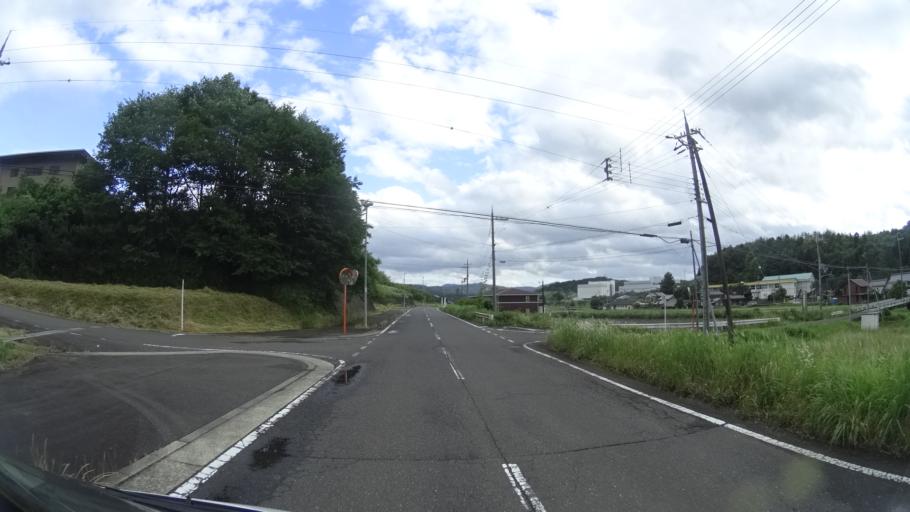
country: JP
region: Kyoto
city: Ayabe
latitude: 35.3373
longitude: 135.2938
